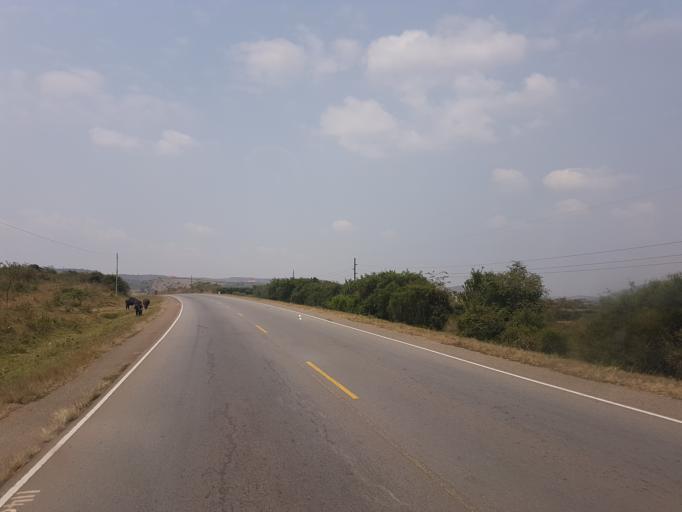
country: UG
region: Western Region
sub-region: Mbarara District
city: Mbarara
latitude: -0.5095
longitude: 30.8375
